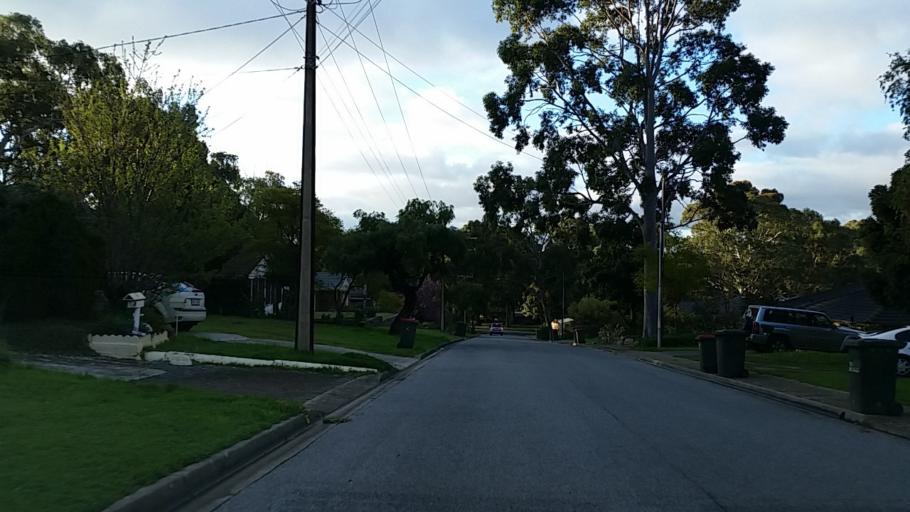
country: AU
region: South Australia
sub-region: Tea Tree Gully
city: Hope Valley
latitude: -34.8462
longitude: 138.7038
